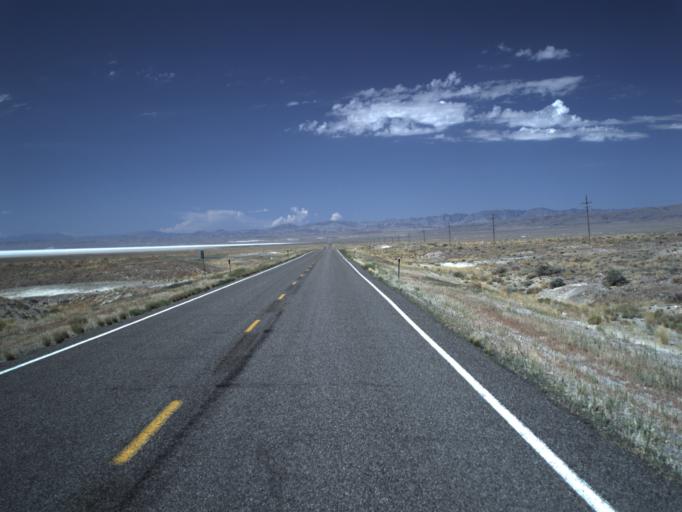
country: US
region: Utah
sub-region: Millard County
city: Delta
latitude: 39.1454
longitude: -113.0776
